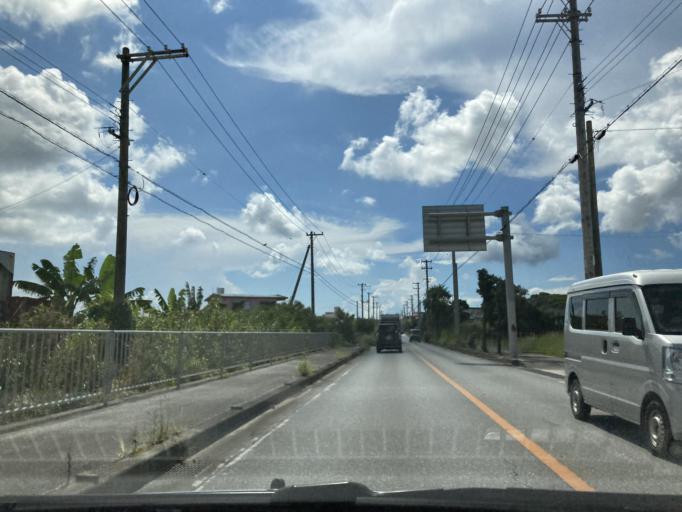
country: JP
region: Okinawa
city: Tomigusuku
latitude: 26.1454
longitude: 127.7261
